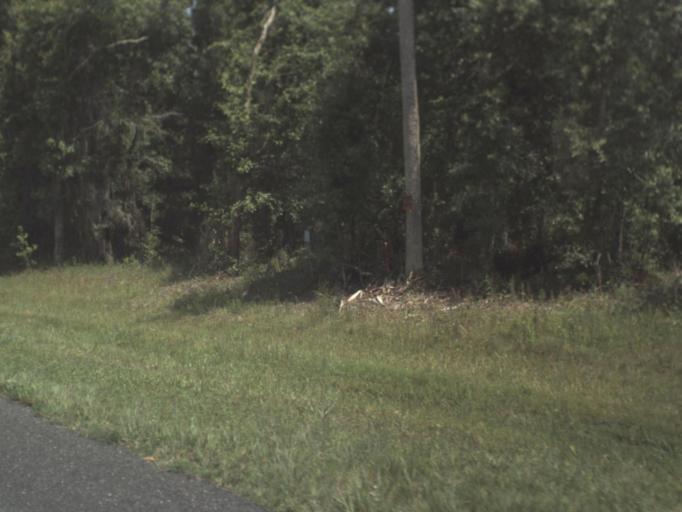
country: US
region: Florida
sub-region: Alachua County
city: Hawthorne
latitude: 29.5979
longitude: -82.1839
